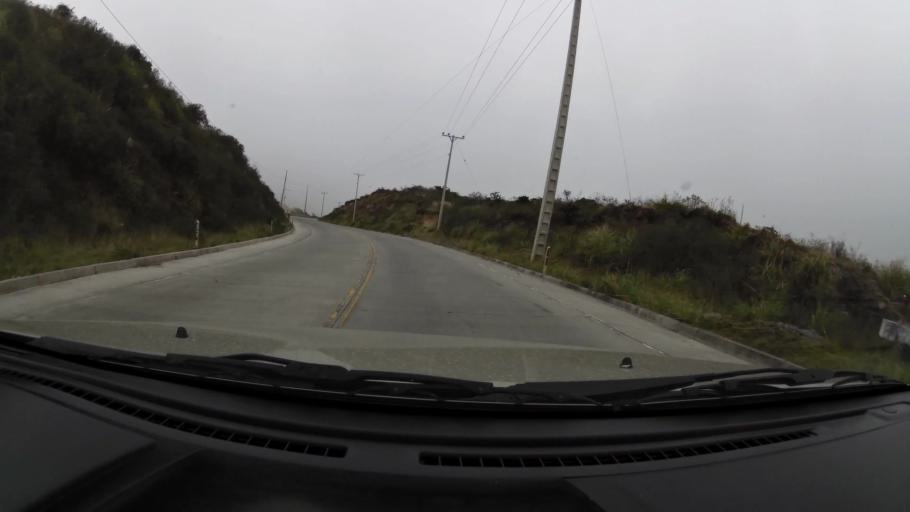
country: EC
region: Canar
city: Canar
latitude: -2.4876
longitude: -79.0023
